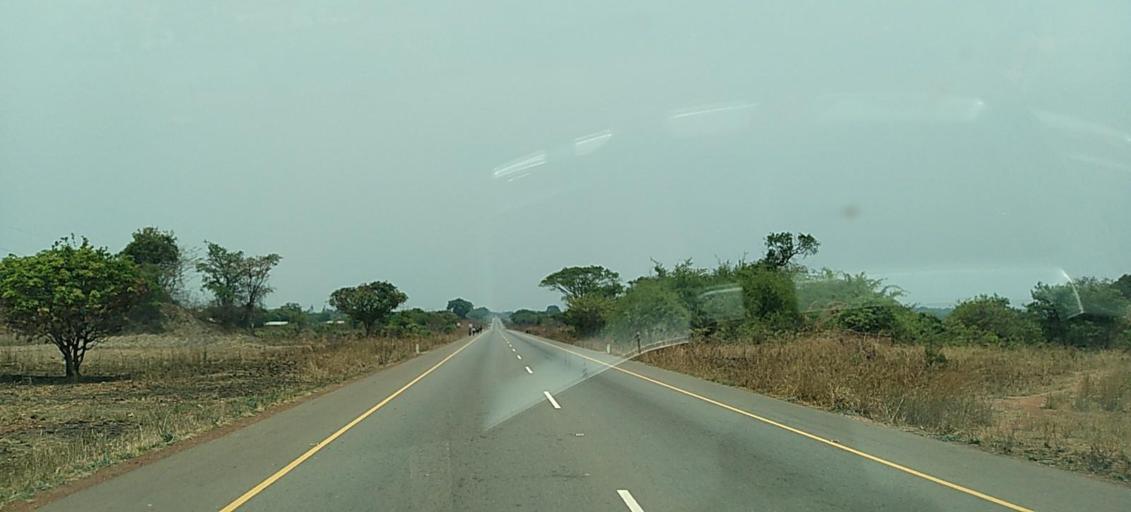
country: ZM
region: Copperbelt
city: Chililabombwe
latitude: -12.5044
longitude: 27.5446
